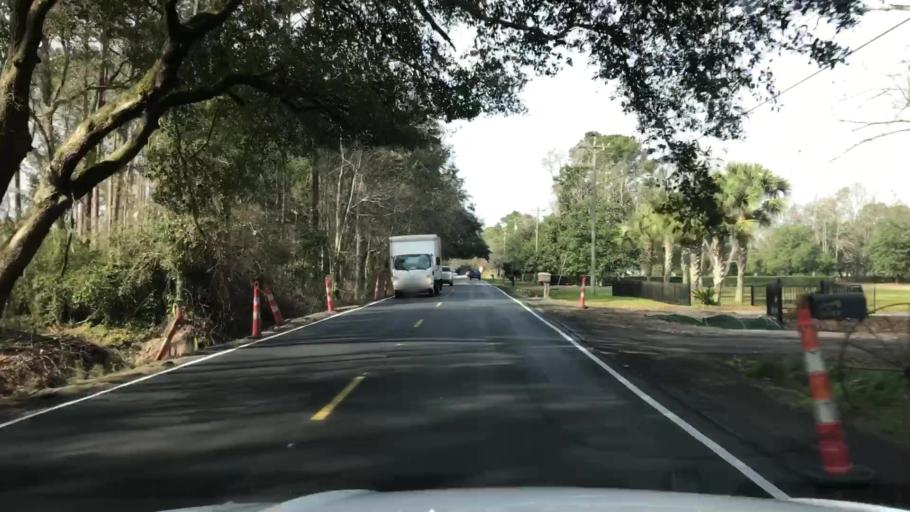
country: US
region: South Carolina
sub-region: Charleston County
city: Shell Point
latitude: 32.7663
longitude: -80.0674
